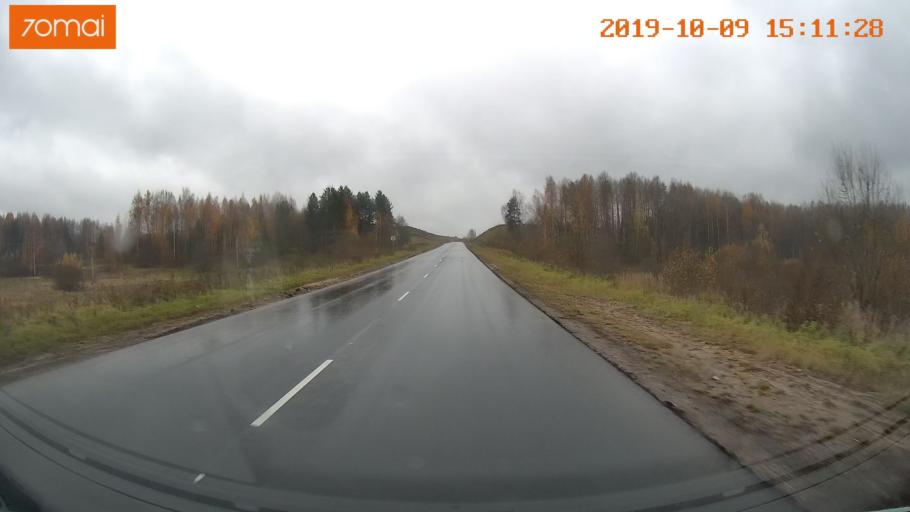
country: RU
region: Kostroma
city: Susanino
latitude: 58.1646
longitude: 41.6298
